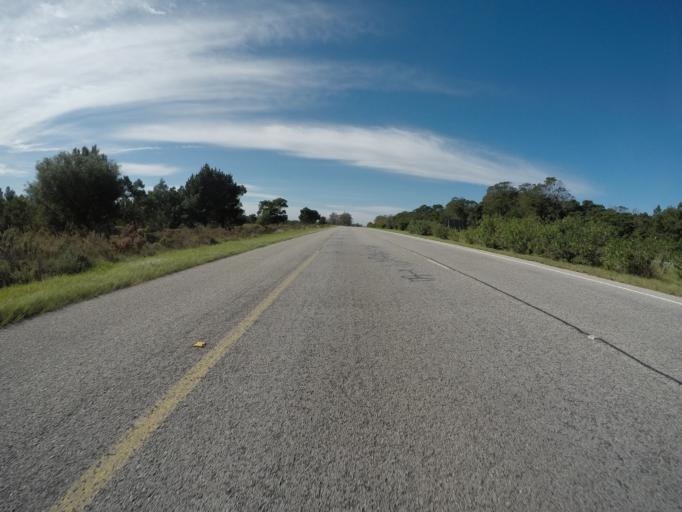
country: ZA
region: Eastern Cape
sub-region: Nelson Mandela Bay Metropolitan Municipality
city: Uitenhage
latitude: -33.9343
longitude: 25.3600
